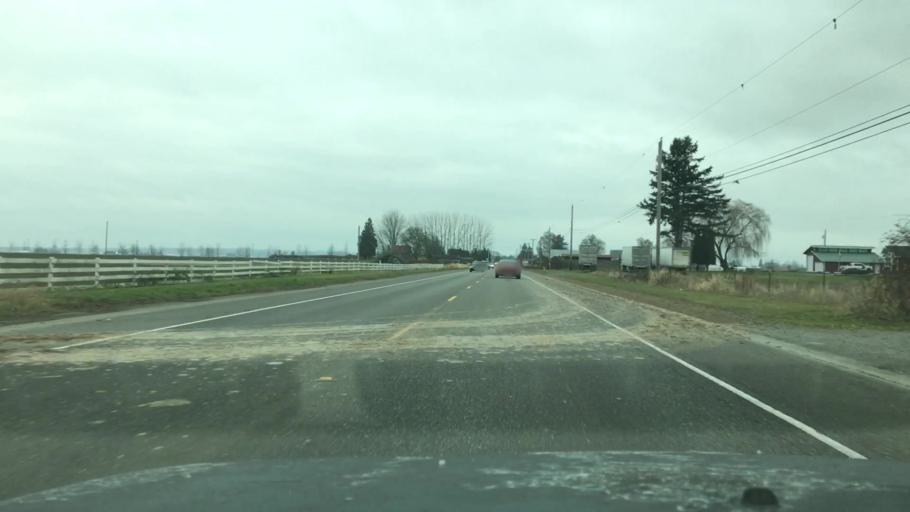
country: US
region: Washington
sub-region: Skagit County
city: Burlington
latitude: 48.5073
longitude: -122.2997
